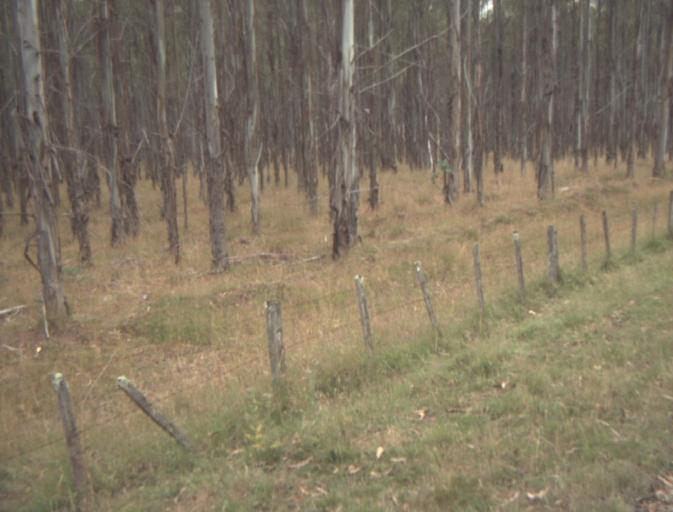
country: AU
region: Tasmania
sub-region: Dorset
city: Scottsdale
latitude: -41.4148
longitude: 147.5207
